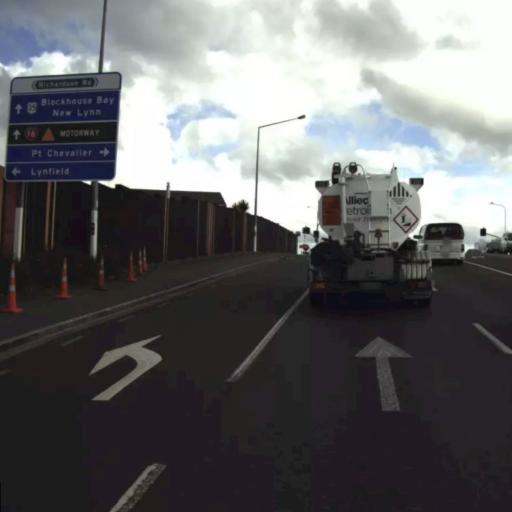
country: NZ
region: Auckland
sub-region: Auckland
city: Auckland
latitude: -36.9045
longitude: 174.7224
